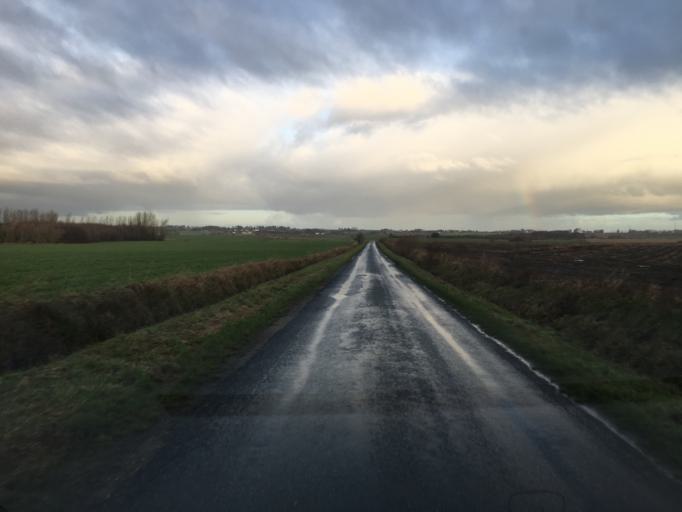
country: DK
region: South Denmark
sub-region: Tonder Kommune
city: Sherrebek
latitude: 55.1360
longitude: 8.8282
